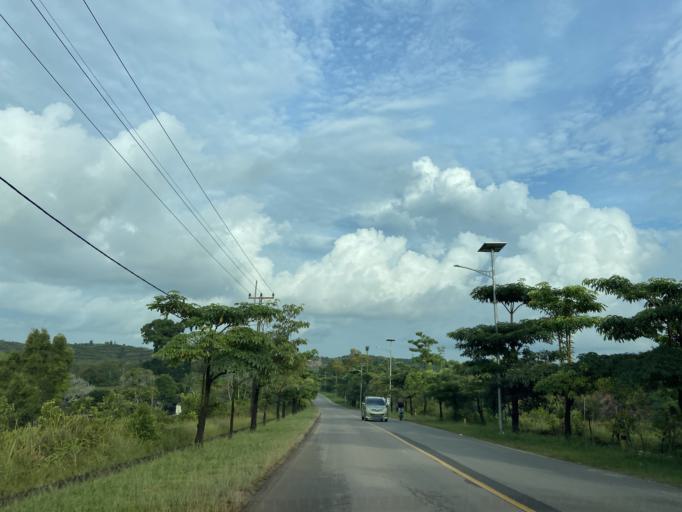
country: ID
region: Riau Islands
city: Tanjungpinang
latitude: 0.9351
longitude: 104.1055
